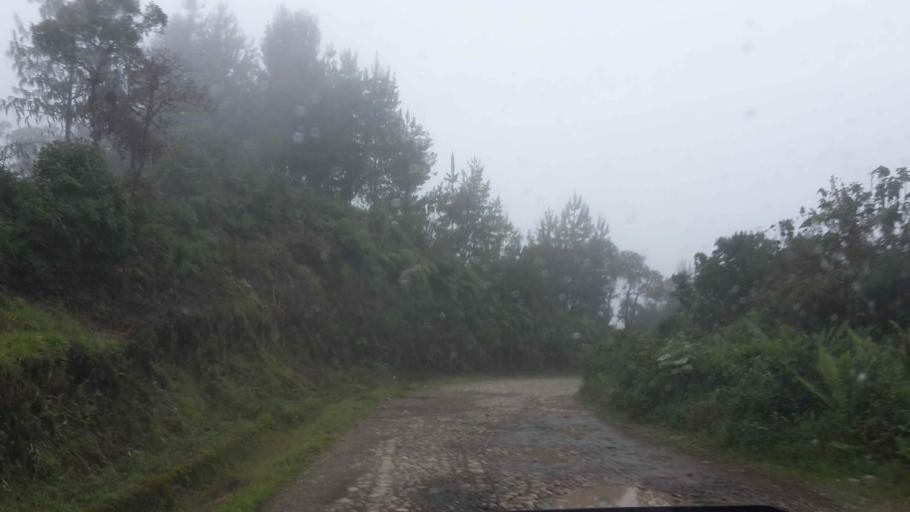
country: BO
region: Cochabamba
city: Colomi
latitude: -17.1219
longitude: -65.9635
